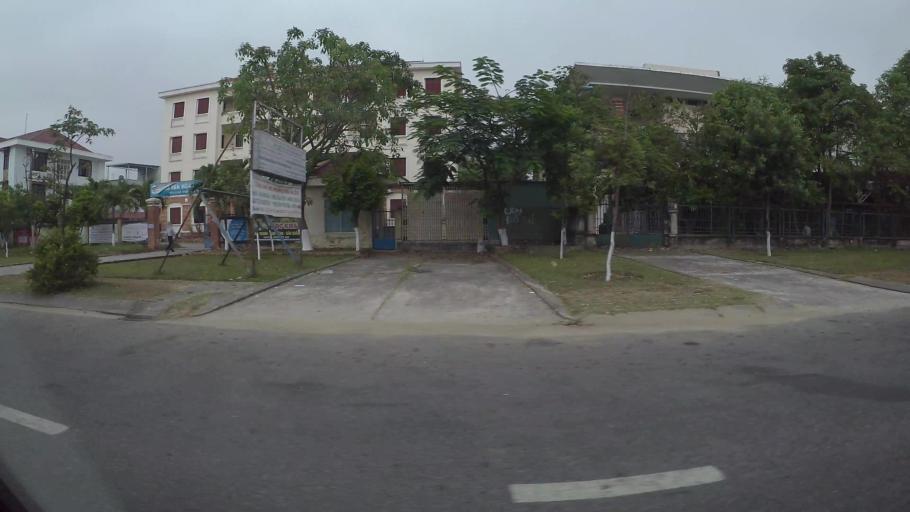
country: VN
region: Da Nang
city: Cam Le
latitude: 16.0272
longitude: 108.2201
